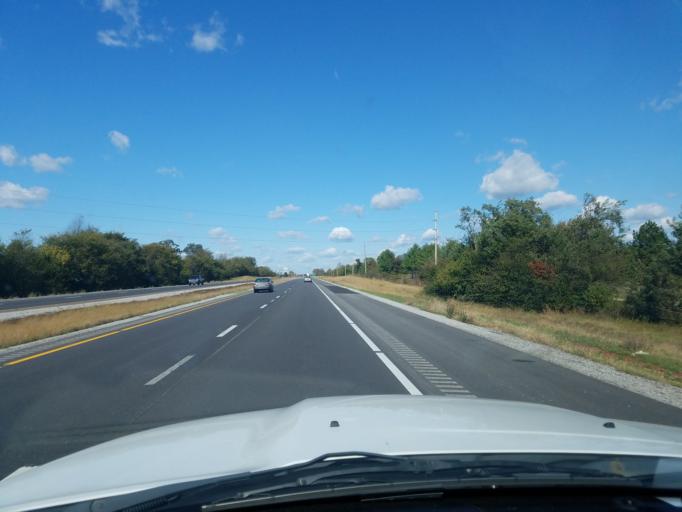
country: US
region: Kentucky
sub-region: Warren County
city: Plano
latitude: 36.9171
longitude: -86.4431
